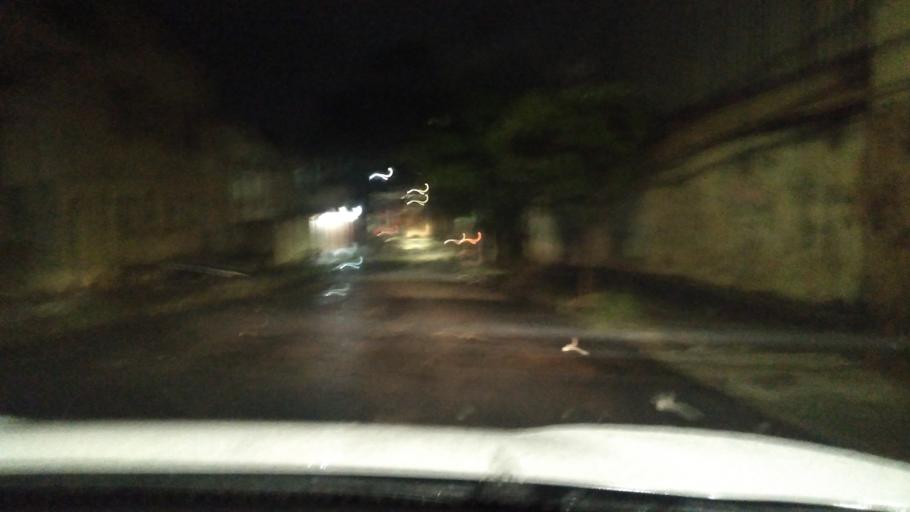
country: BR
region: Minas Gerais
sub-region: Belo Horizonte
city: Belo Horizonte
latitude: -19.9111
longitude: -43.9489
